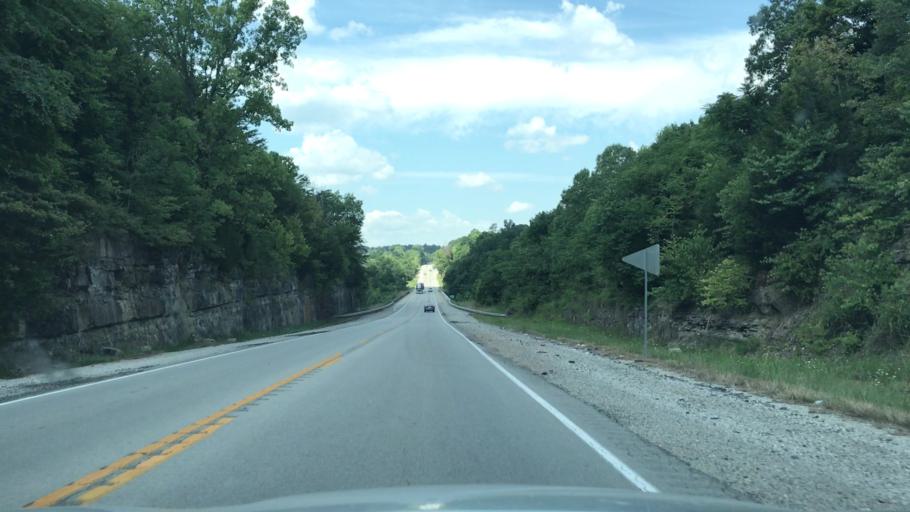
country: US
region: Kentucky
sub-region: Wayne County
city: Monticello
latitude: 36.7652
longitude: -84.9708
